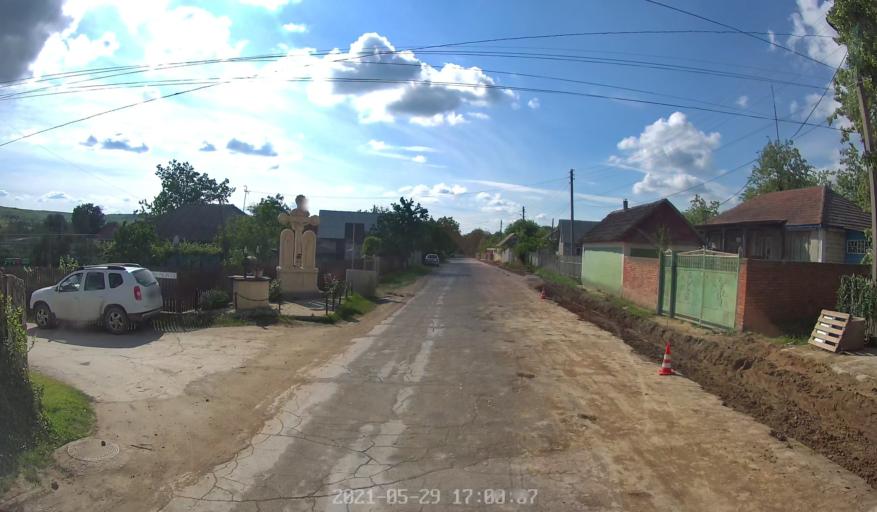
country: MD
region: Chisinau
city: Singera
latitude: 46.8281
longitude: 28.8679
